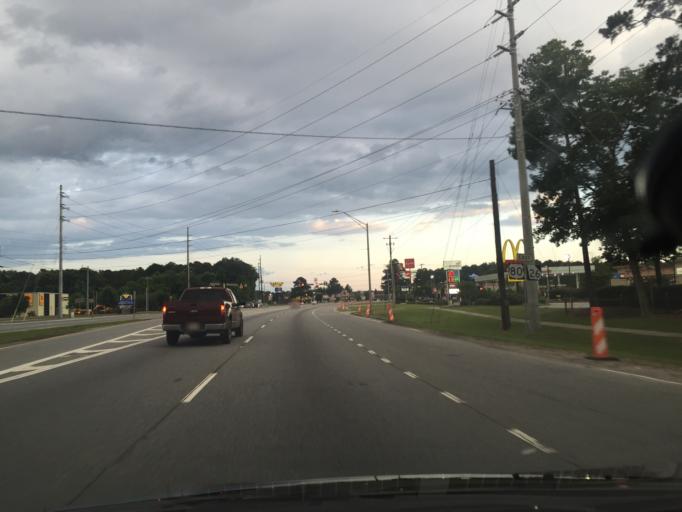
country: US
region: Georgia
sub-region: Chatham County
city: Pooler
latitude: 32.1120
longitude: -81.2366
